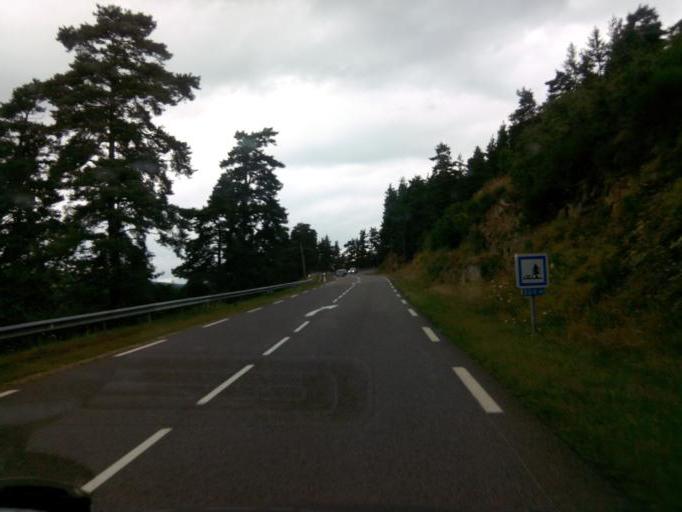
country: FR
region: Rhone-Alpes
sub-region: Departement de la Loire
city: Usson-en-Forez
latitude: 45.3565
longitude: 3.8995
